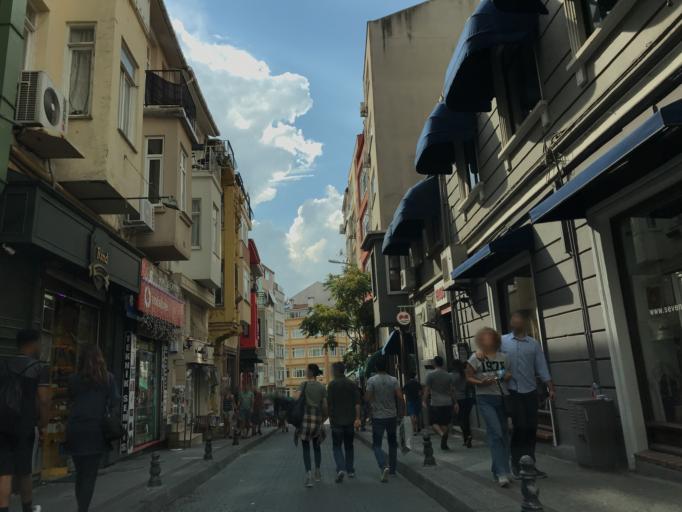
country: TR
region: Istanbul
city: UEskuedar
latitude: 40.9878
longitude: 29.0253
